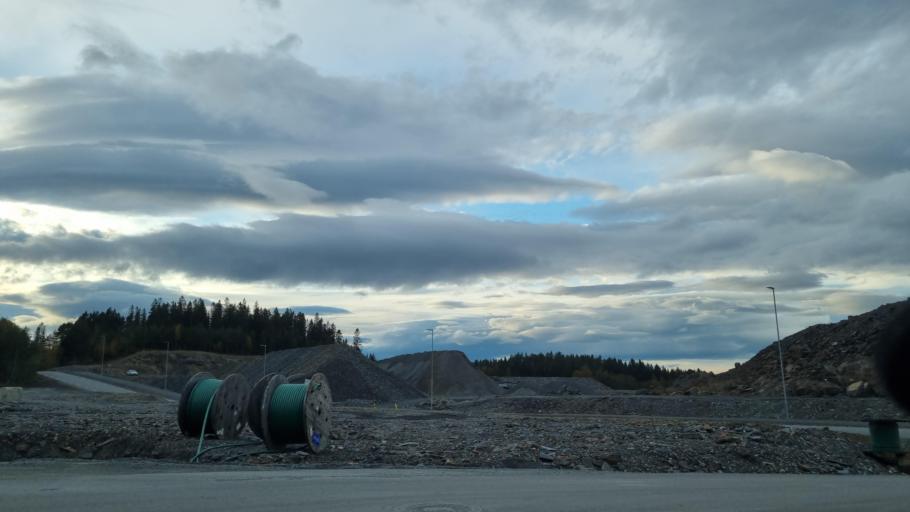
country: NO
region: Sor-Trondelag
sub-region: Malvik
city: Malvik
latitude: 63.4208
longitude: 10.7265
